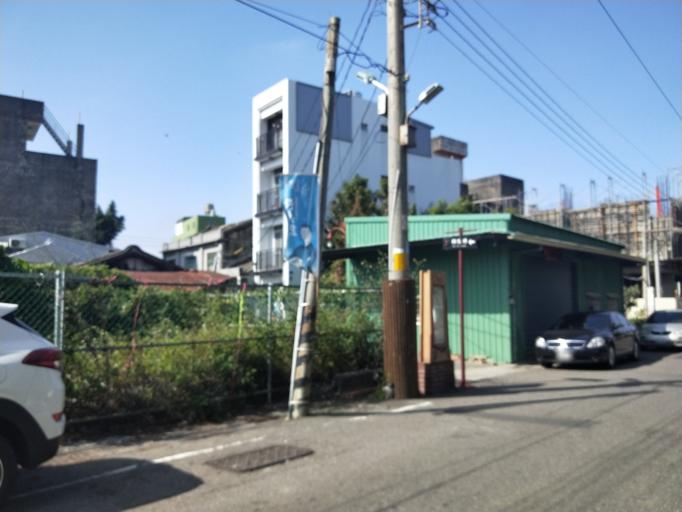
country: TW
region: Taiwan
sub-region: Changhua
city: Chang-hua
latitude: 24.0514
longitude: 120.4333
